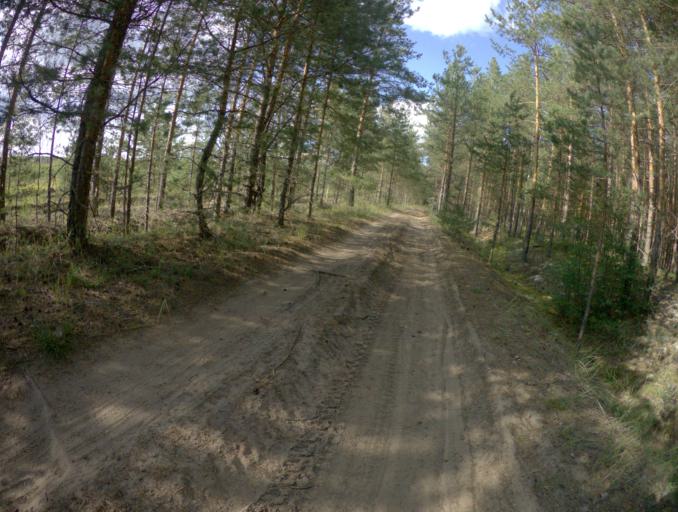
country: RU
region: Vladimir
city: Sobinka
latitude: 55.9564
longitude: 40.0608
